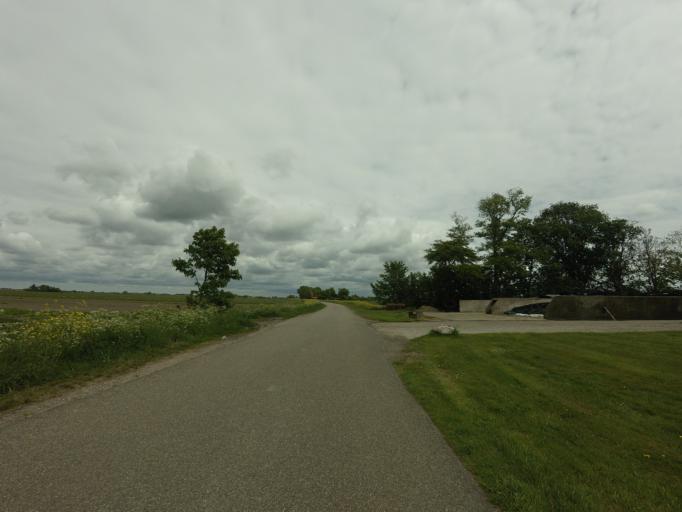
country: NL
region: Friesland
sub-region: Sudwest Fryslan
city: Woudsend
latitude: 52.9489
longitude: 5.6095
